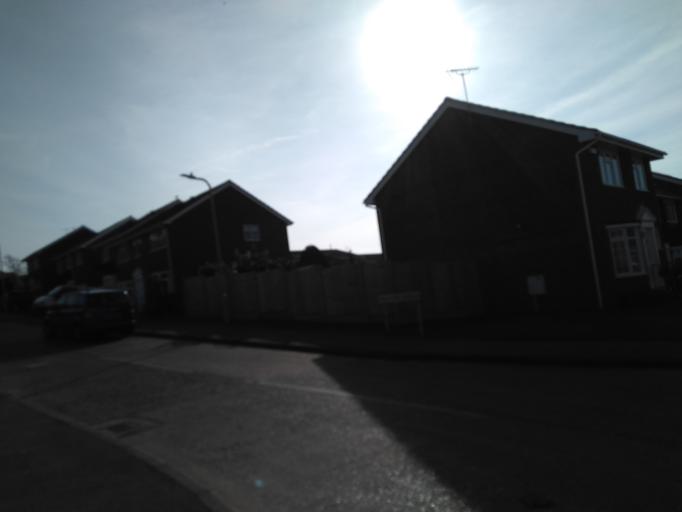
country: GB
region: England
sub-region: Kent
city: Whitstable
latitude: 51.3457
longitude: 1.0124
